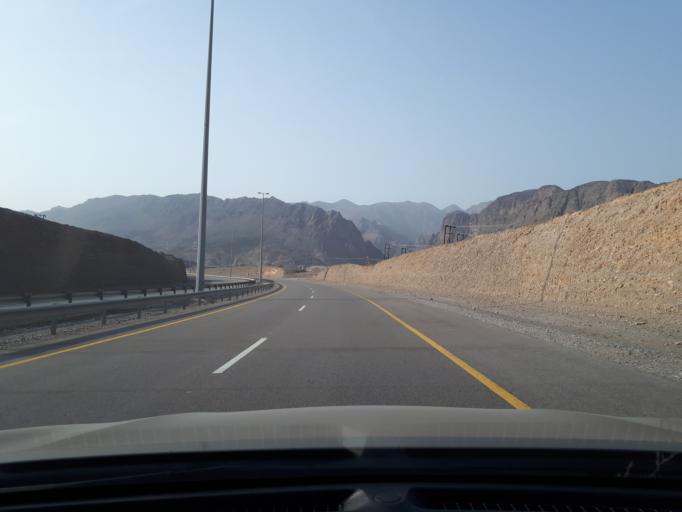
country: OM
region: Muhafazat Masqat
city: Muscat
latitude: 23.2410
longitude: 58.7940
